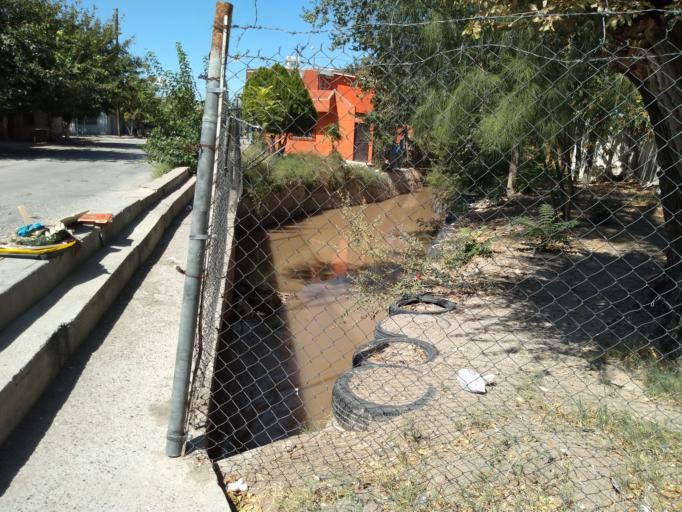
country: US
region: Texas
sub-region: El Paso County
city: El Paso
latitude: 31.7457
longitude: -106.4914
